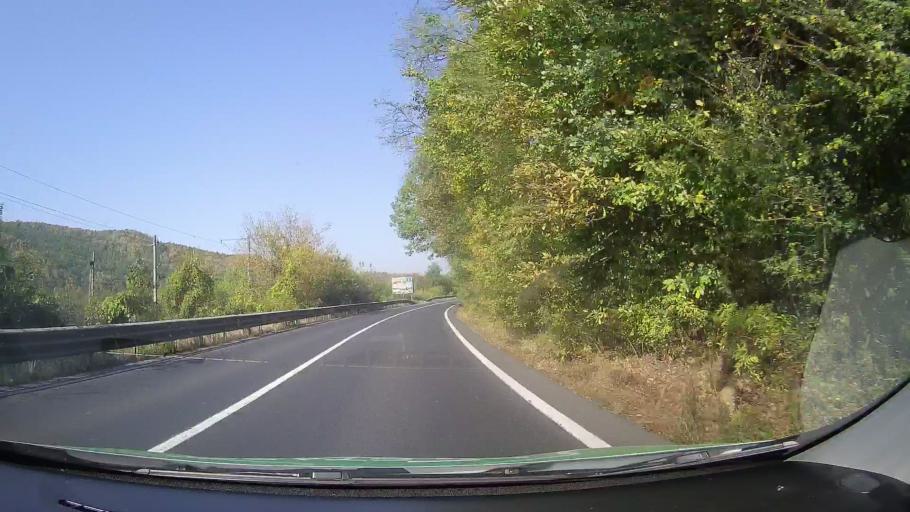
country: RO
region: Hunedoara
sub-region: Comuna Zam
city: Zam
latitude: 45.9761
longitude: 22.4325
